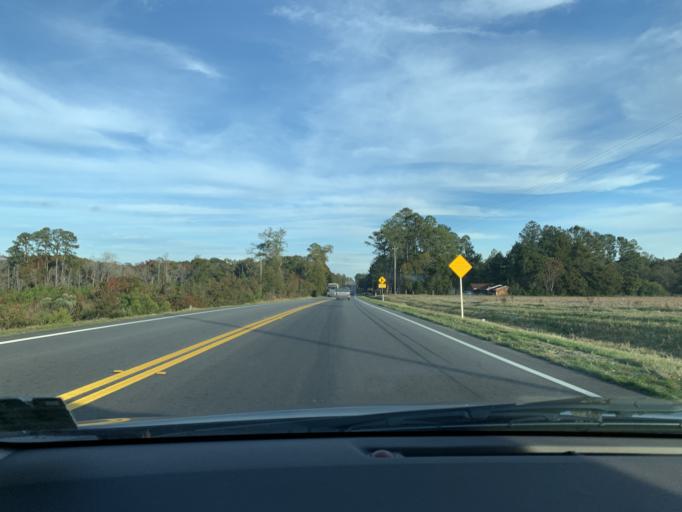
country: US
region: Georgia
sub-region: Irwin County
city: Ocilla
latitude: 31.5960
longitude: -83.1771
